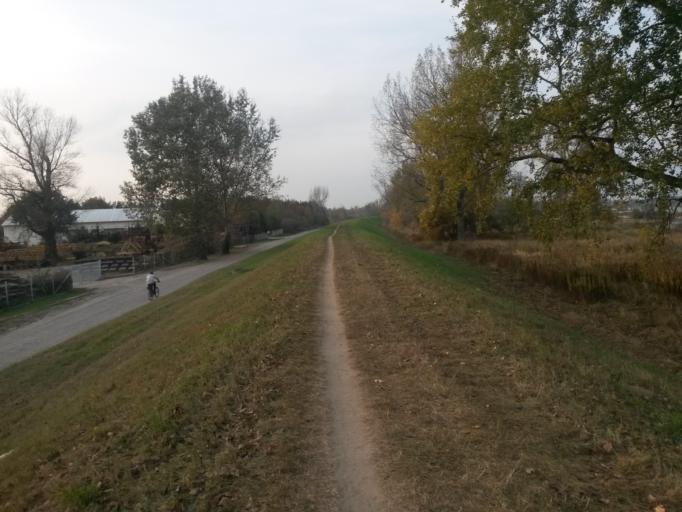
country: PL
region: Masovian Voivodeship
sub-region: Warszawa
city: Wawer
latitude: 52.1404
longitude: 21.1585
